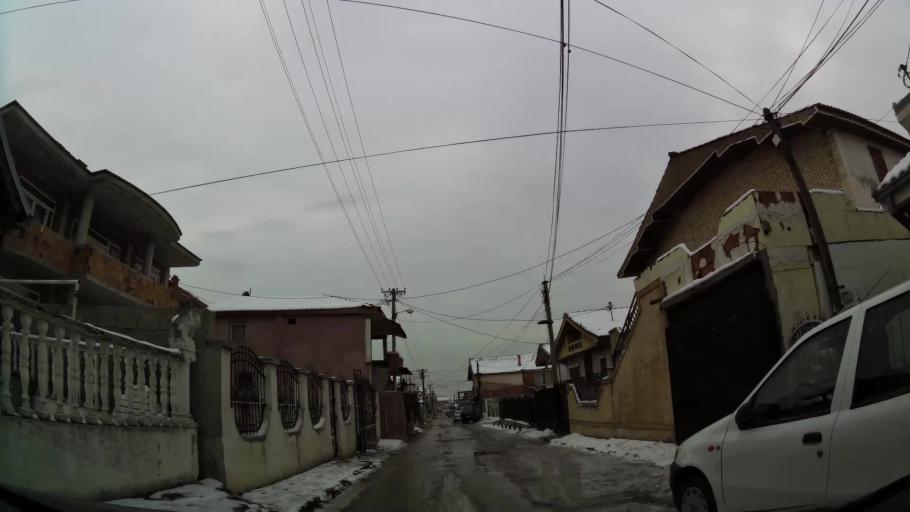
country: MK
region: Suto Orizari
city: Suto Orizare
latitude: 42.0378
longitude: 21.4223
